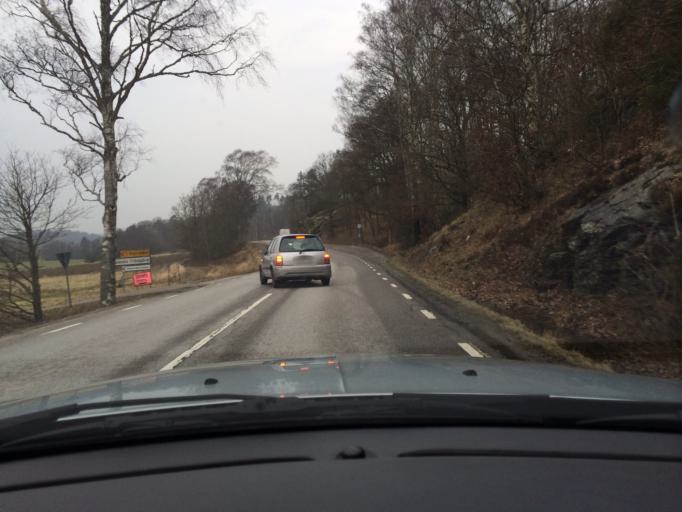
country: SE
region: Vaestra Goetaland
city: Svanesund
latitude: 58.1179
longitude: 11.8544
